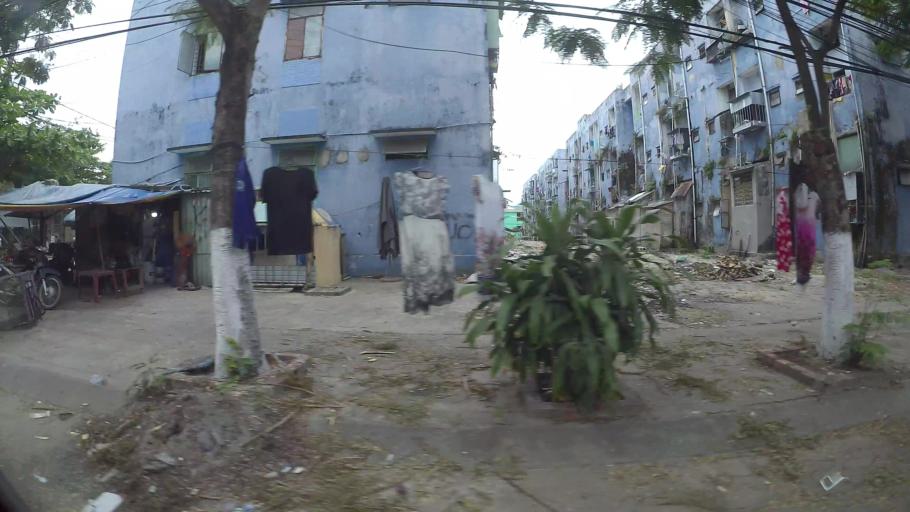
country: VN
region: Da Nang
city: Lien Chieu
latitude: 16.0791
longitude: 108.1678
